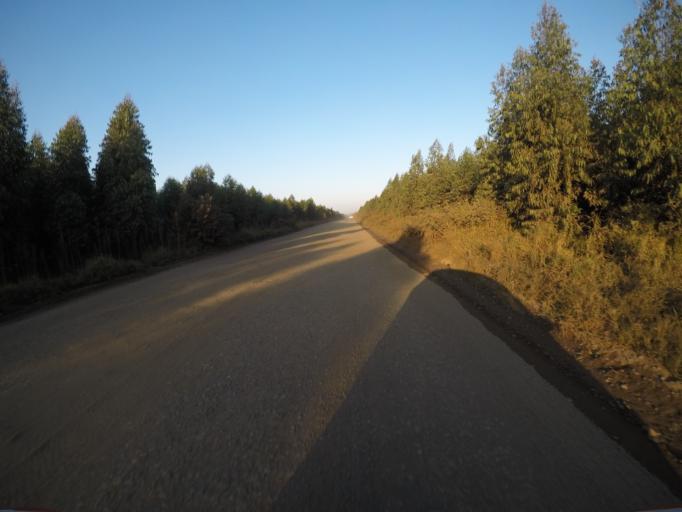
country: ZA
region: KwaZulu-Natal
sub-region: uThungulu District Municipality
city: KwaMbonambi
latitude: -28.6658
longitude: 32.0636
